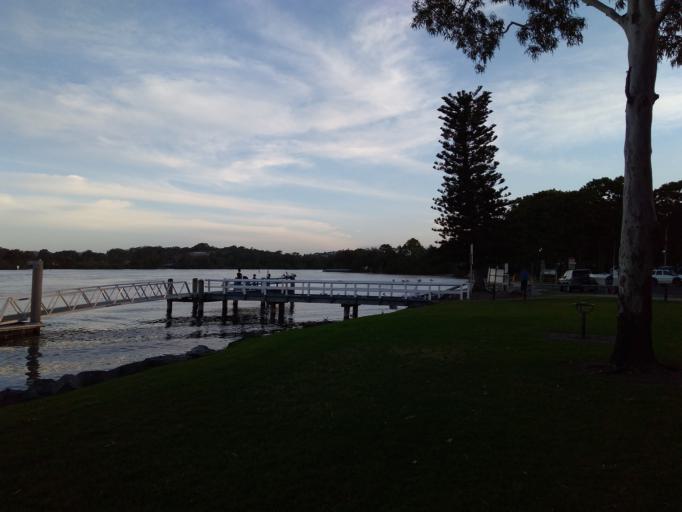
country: AU
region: New South Wales
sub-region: Tweed
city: Tweed Heads West
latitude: -28.1864
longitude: 153.5323
